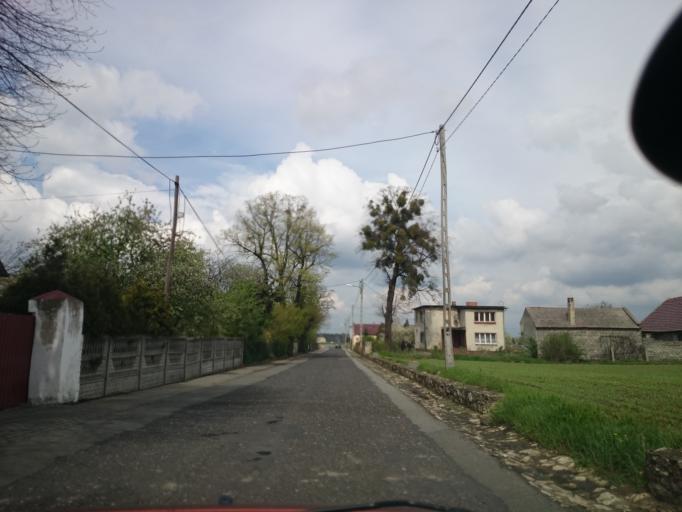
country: PL
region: Opole Voivodeship
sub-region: Powiat krapkowicki
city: Rozwadza
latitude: 50.4926
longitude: 18.1203
